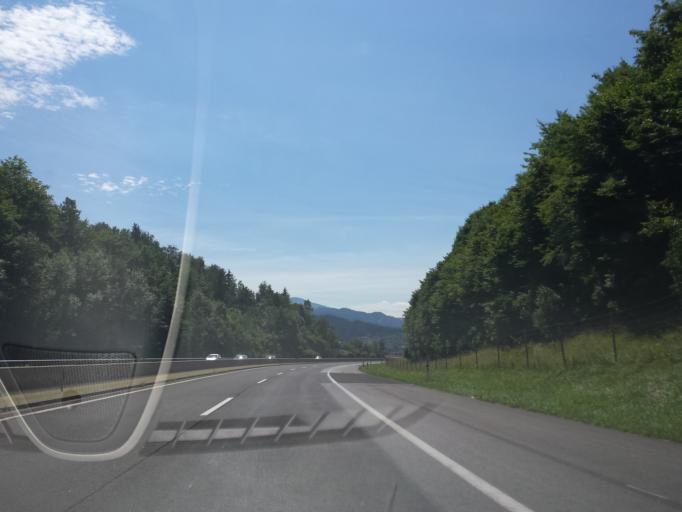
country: AT
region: Styria
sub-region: Politischer Bezirk Bruck-Muerzzuschlag
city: Kindberg
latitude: 47.5063
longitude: 15.4473
